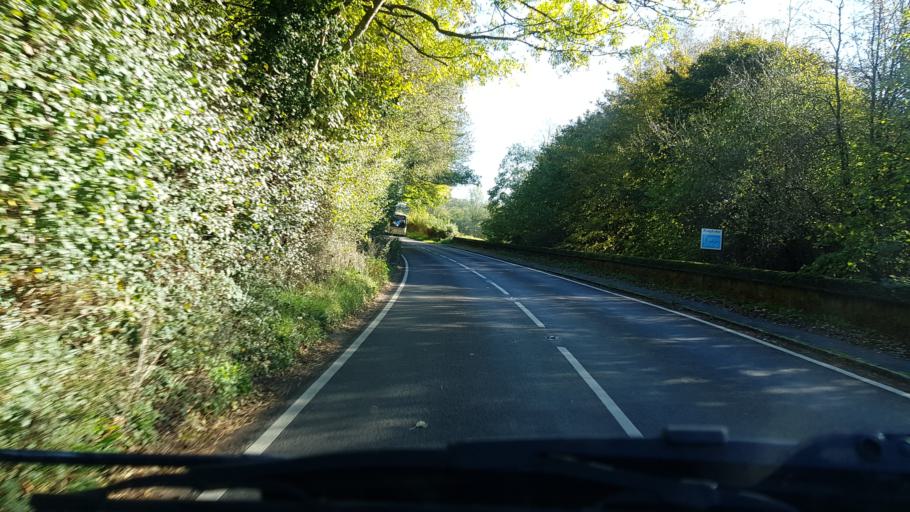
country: GB
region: England
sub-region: Surrey
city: East Horsley
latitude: 51.2151
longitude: -0.4291
